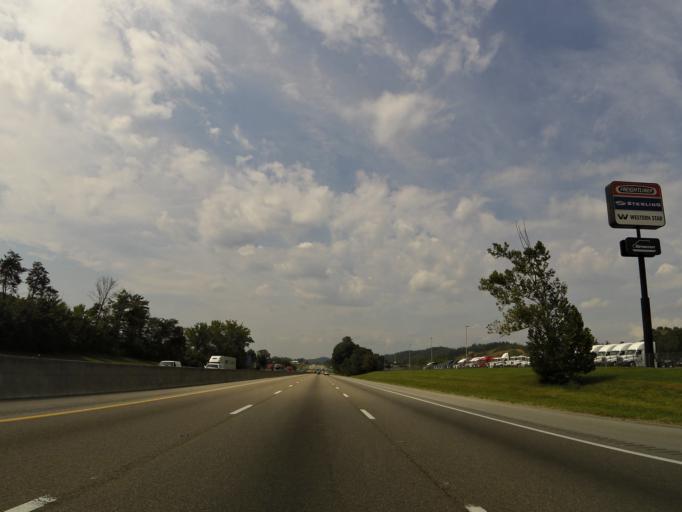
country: US
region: Tennessee
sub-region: Knox County
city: Farragut
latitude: 35.8834
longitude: -84.2267
